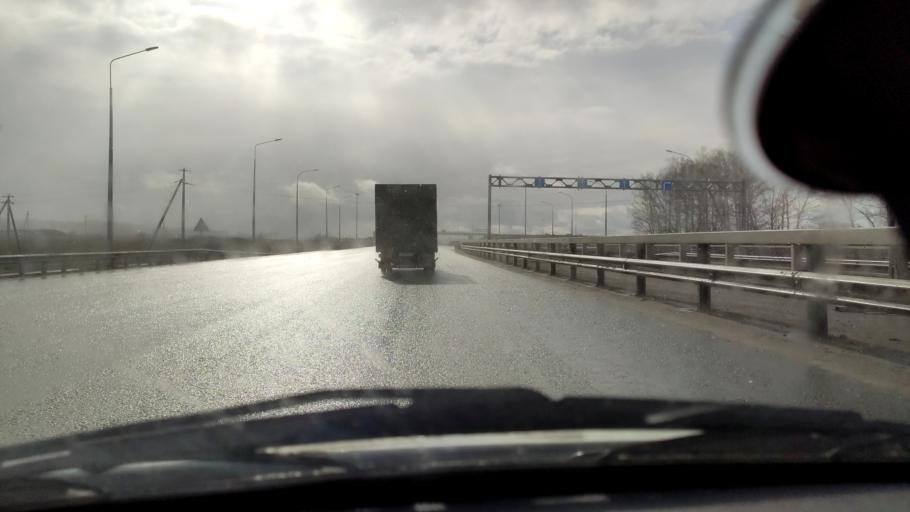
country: RU
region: Bashkortostan
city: Buzdyak
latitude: 54.6439
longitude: 54.5449
